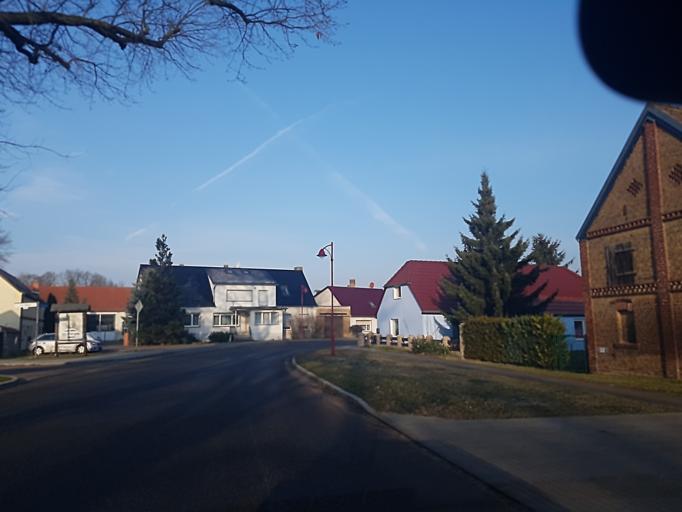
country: DE
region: Brandenburg
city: Golzow
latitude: 52.2585
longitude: 12.6596
